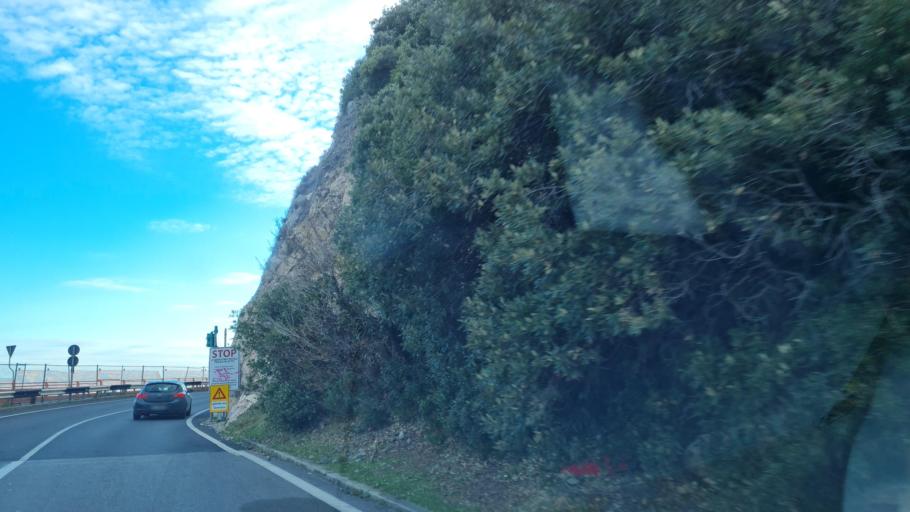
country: IT
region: Liguria
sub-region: Provincia di Savona
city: Noli
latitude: 44.1972
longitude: 8.4245
